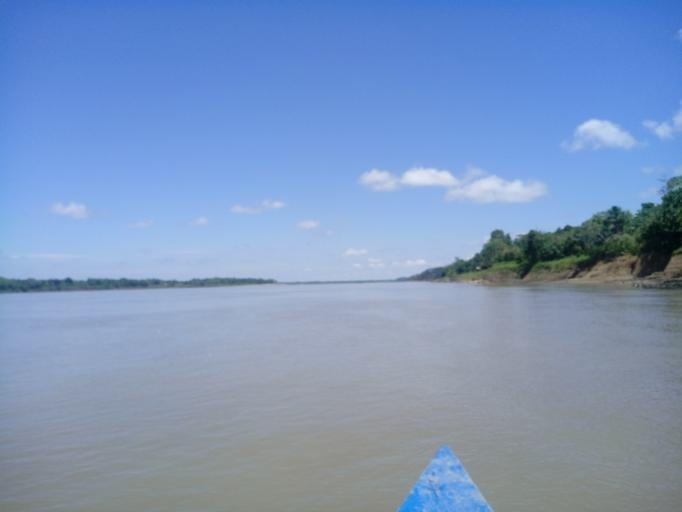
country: PE
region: Loreto
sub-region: Provincia de Loreto
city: Nauta
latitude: -4.5745
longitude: -73.7051
